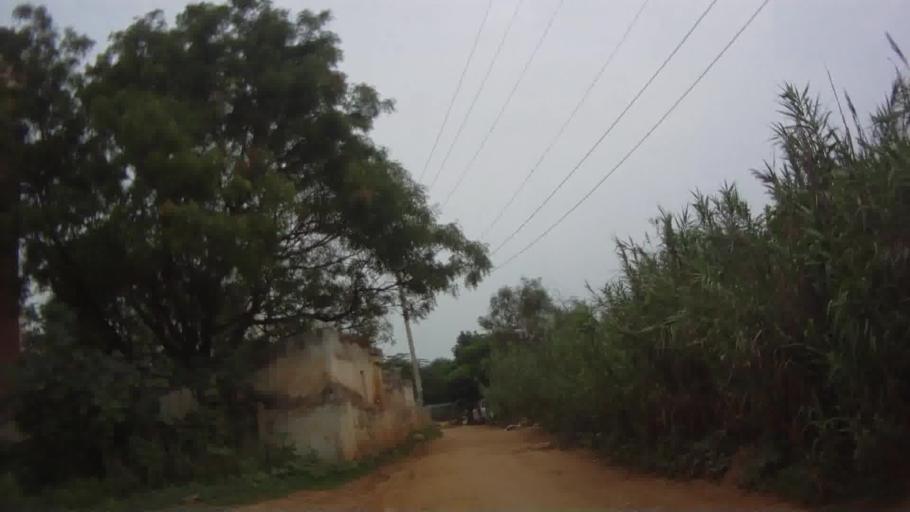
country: IN
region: Karnataka
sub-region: Bangalore Urban
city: Bangalore
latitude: 12.9689
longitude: 77.7030
